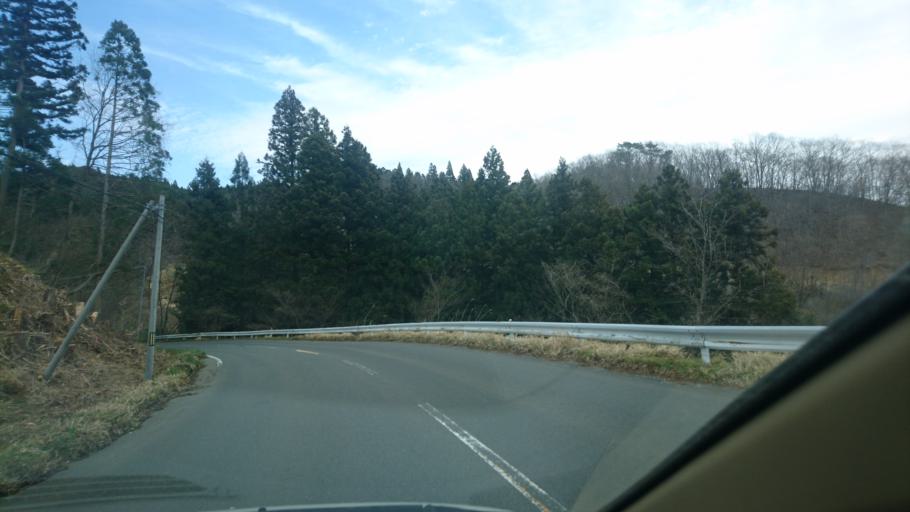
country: JP
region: Miyagi
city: Furukawa
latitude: 38.7207
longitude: 140.8319
